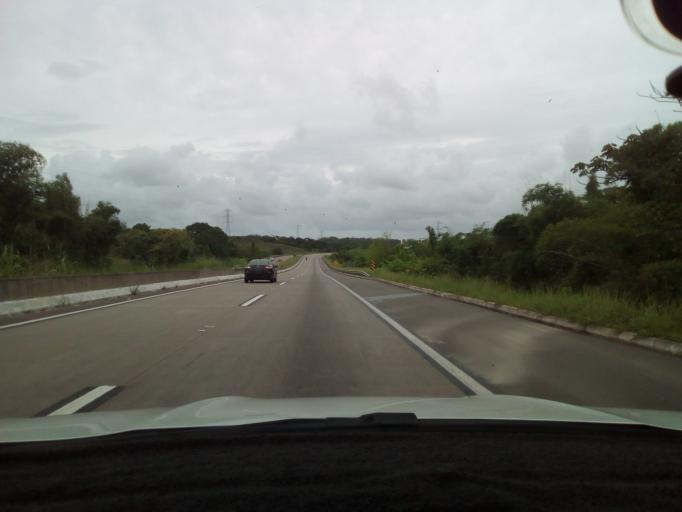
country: BR
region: Paraiba
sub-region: Conde
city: Conde
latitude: -7.3172
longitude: -34.9465
